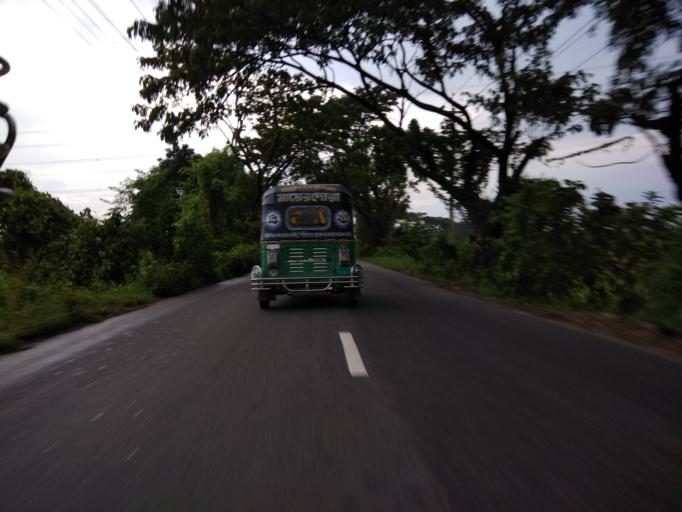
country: BD
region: Dhaka
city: Azimpur
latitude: 23.6956
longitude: 90.3190
